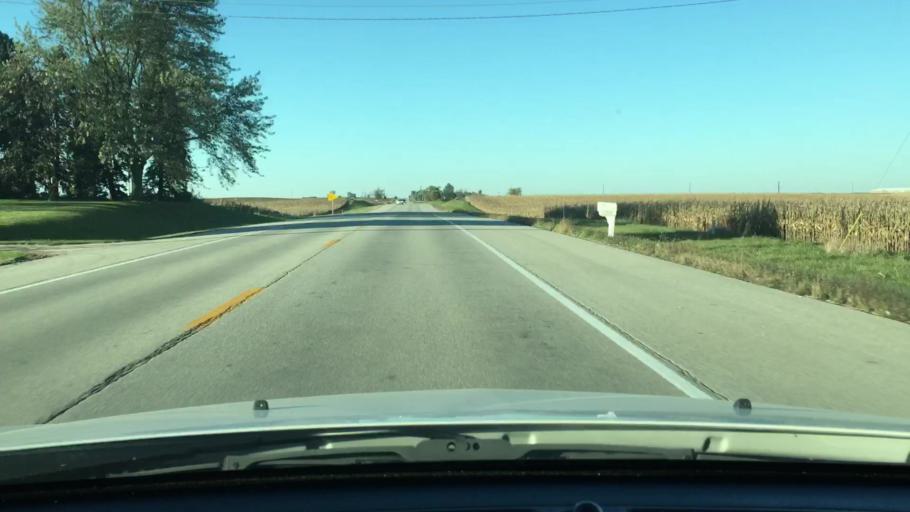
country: US
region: Illinois
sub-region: DeKalb County
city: Waterman
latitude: 41.8099
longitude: -88.7539
